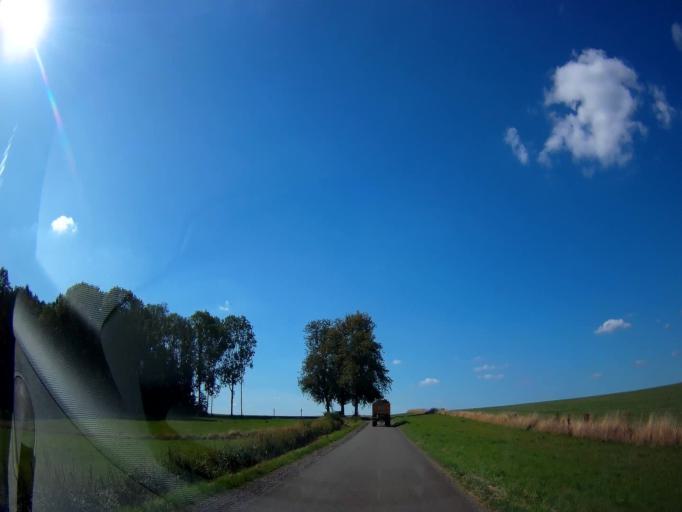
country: BE
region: Wallonia
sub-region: Province de Namur
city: Dinant
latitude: 50.2358
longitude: 4.9698
